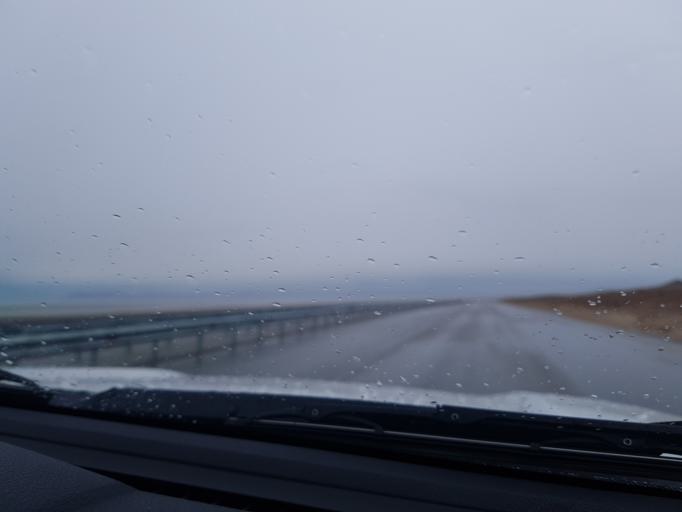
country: TM
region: Balkan
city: Turkmenbasy
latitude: 40.0348
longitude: 53.4765
